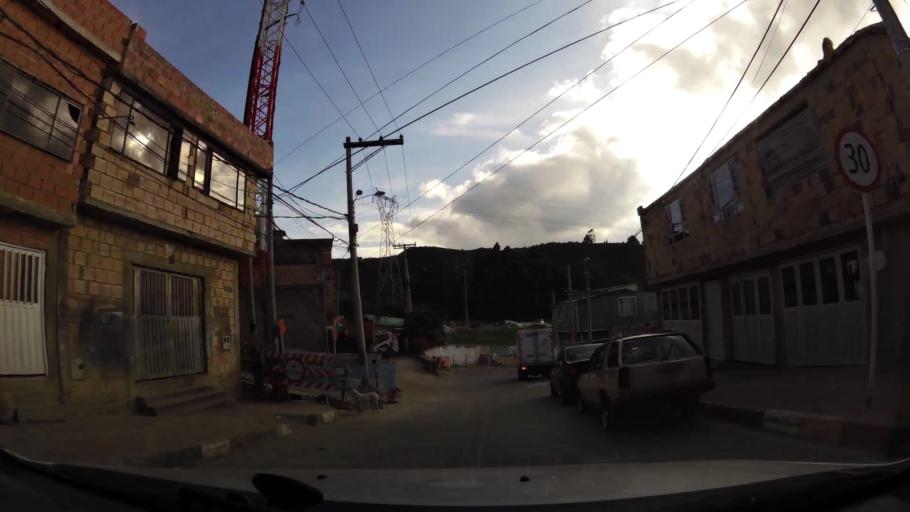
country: CO
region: Bogota D.C.
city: Bogota
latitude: 4.5359
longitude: -74.0928
